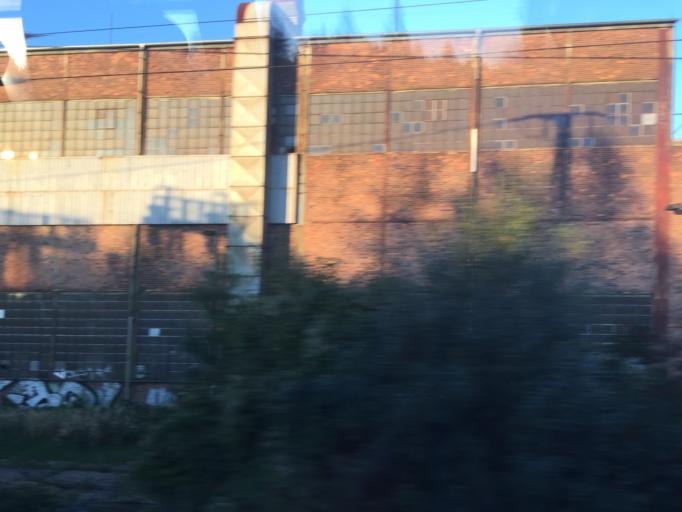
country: DE
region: Saxony
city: Heidenau
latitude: 50.9967
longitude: 13.8336
